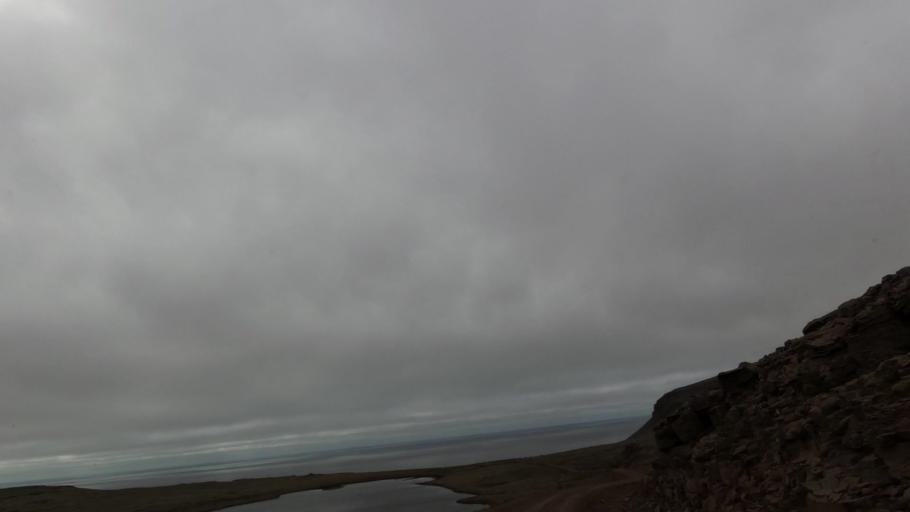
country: IS
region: West
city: Olafsvik
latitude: 65.5259
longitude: -24.4283
